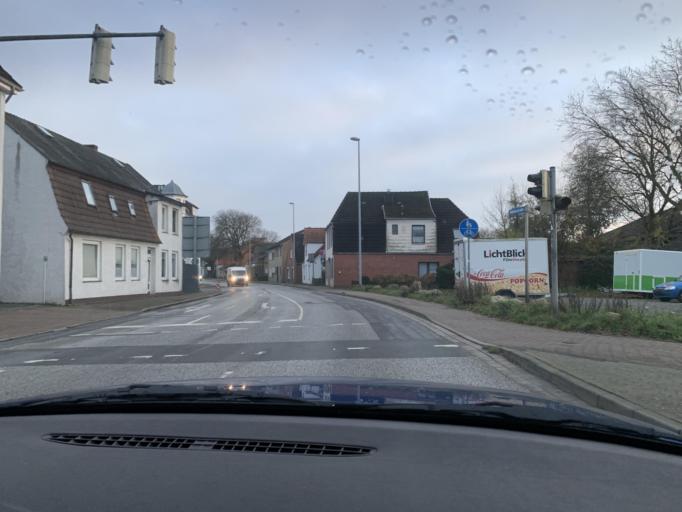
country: DE
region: Schleswig-Holstein
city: Wesseln
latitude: 54.1934
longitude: 9.0866
